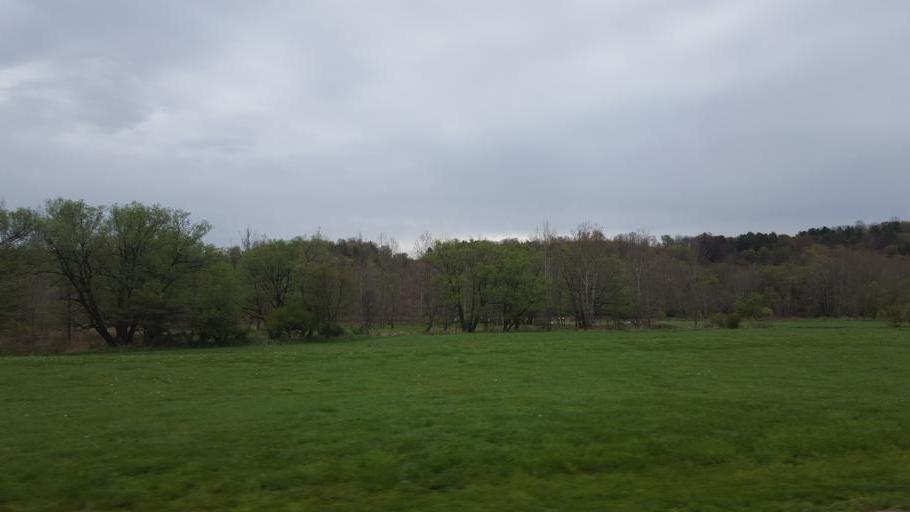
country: US
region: Pennsylvania
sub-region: Tioga County
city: Westfield
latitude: 41.9861
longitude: -77.4824
